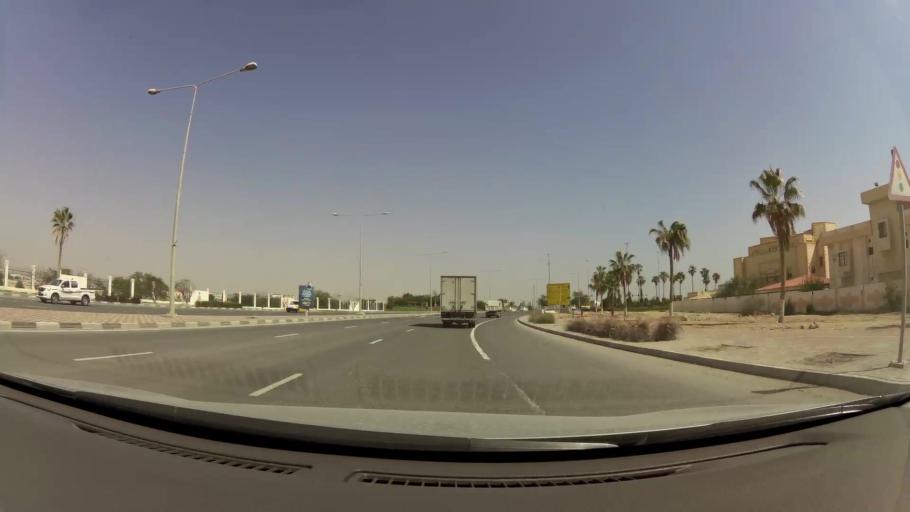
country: QA
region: Baladiyat ad Dawhah
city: Doha
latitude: 25.3641
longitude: 51.4952
